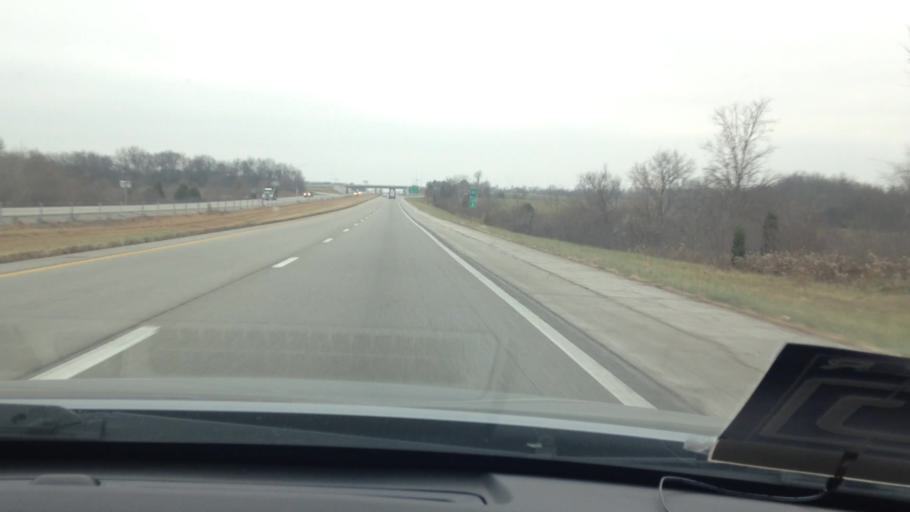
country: US
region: Missouri
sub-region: Cass County
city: Peculiar
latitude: 38.7335
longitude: -94.4646
